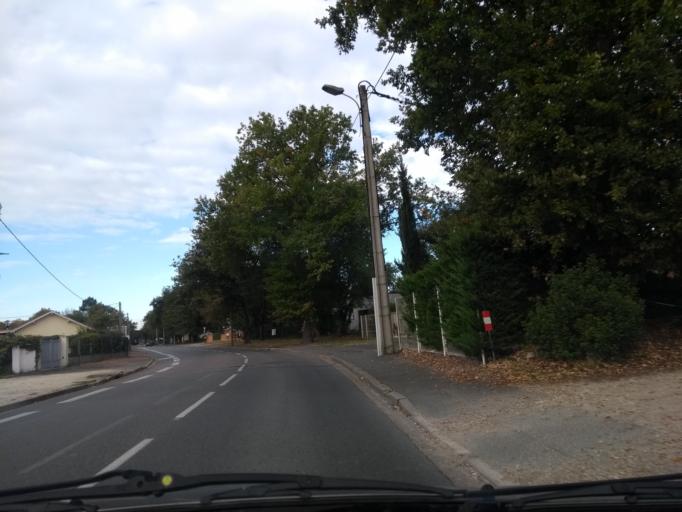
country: FR
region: Aquitaine
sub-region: Departement de la Gironde
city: Canejan
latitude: 44.7737
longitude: -0.6359
